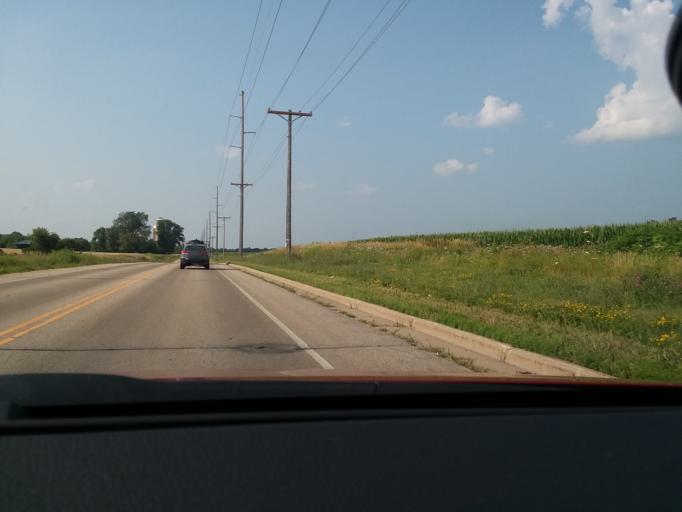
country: US
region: Wisconsin
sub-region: Dane County
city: Cottage Grove
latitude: 43.1090
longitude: -89.2666
